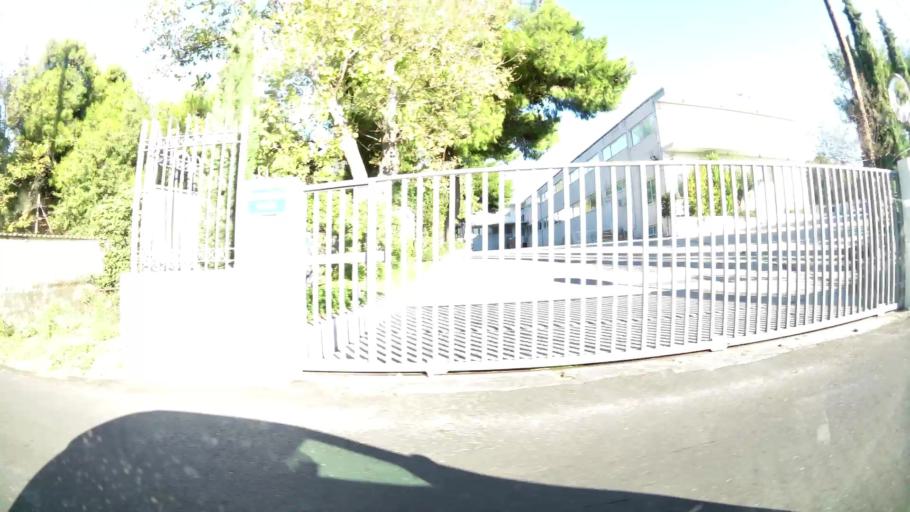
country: GR
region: Attica
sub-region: Nomarchia Anatolikis Attikis
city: Pallini
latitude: 38.0088
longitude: 23.8884
